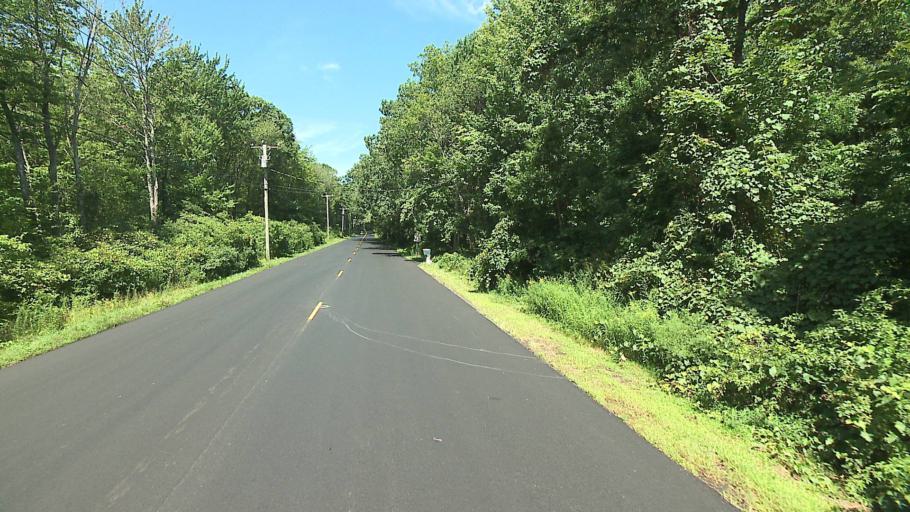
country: US
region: Connecticut
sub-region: Hartford County
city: West Simsbury
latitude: 41.9285
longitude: -72.9136
